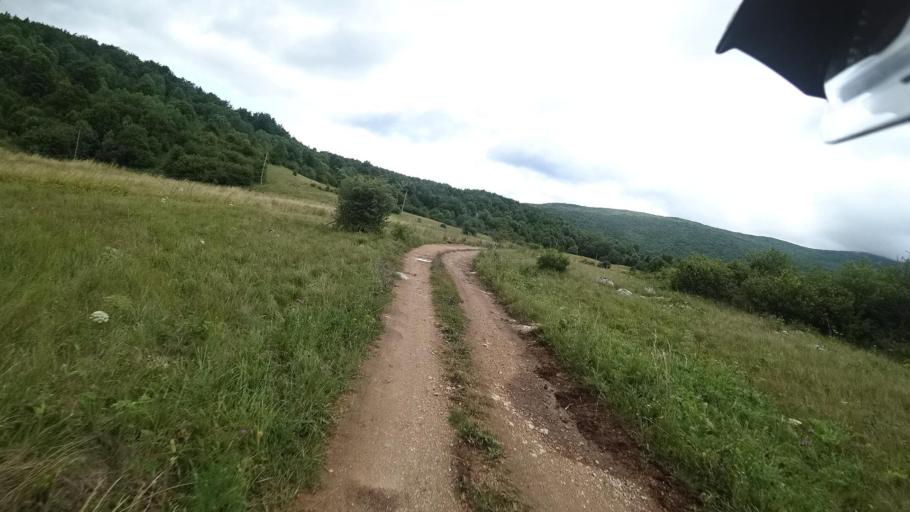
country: HR
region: Licko-Senjska
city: Jezerce
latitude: 44.7748
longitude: 15.4872
